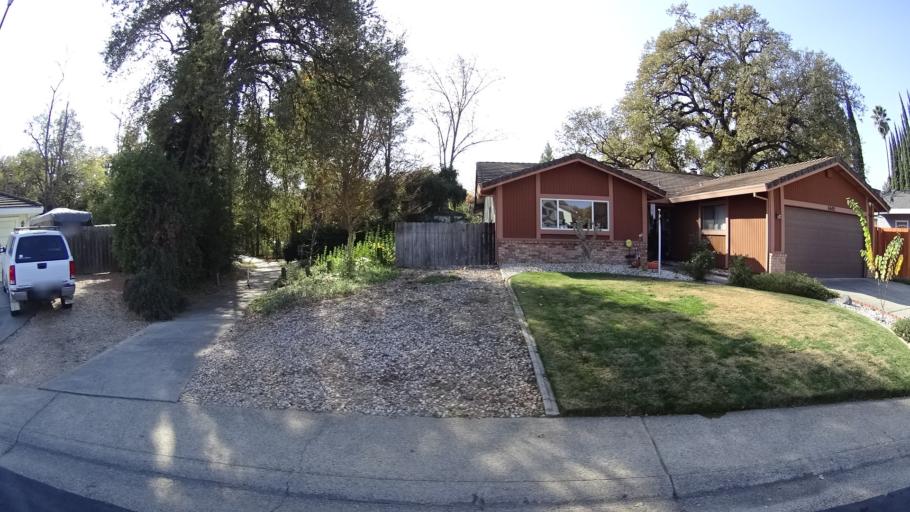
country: US
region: California
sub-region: Sacramento County
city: Citrus Heights
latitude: 38.6873
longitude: -121.2679
